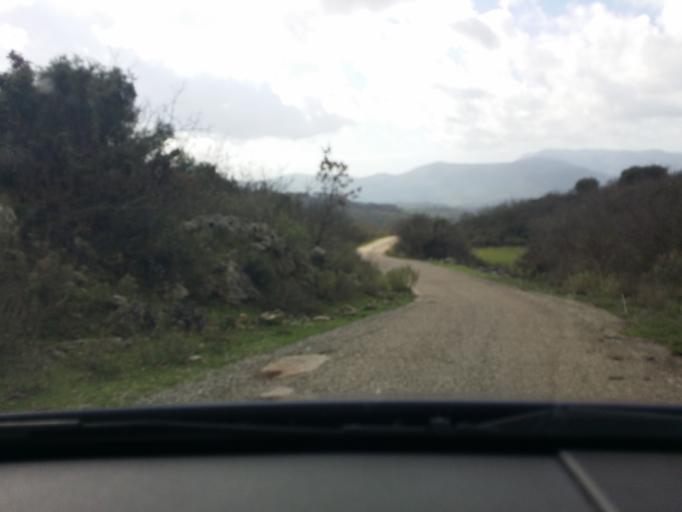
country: GR
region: West Greece
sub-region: Nomos Aitolias kai Akarnanias
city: Fitiai
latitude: 38.6462
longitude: 21.1975
